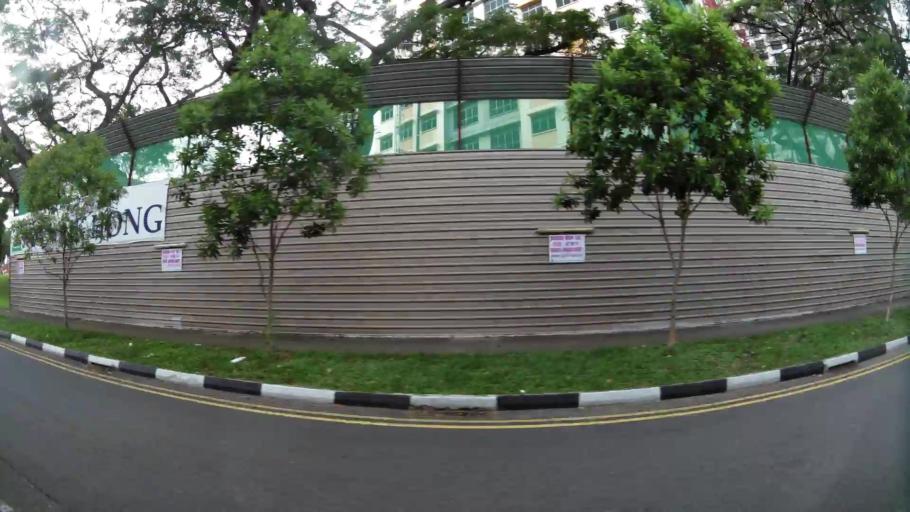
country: SG
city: Singapore
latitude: 1.3323
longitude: 103.8554
